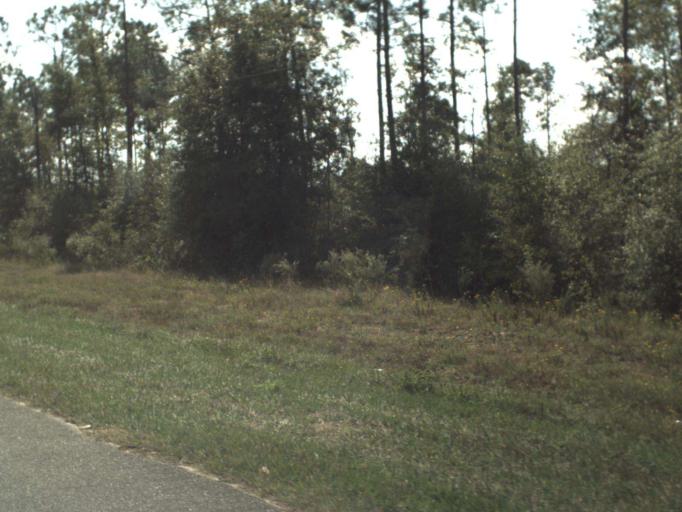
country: US
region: Florida
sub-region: Holmes County
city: Bonifay
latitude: 30.7287
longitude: -85.6855
